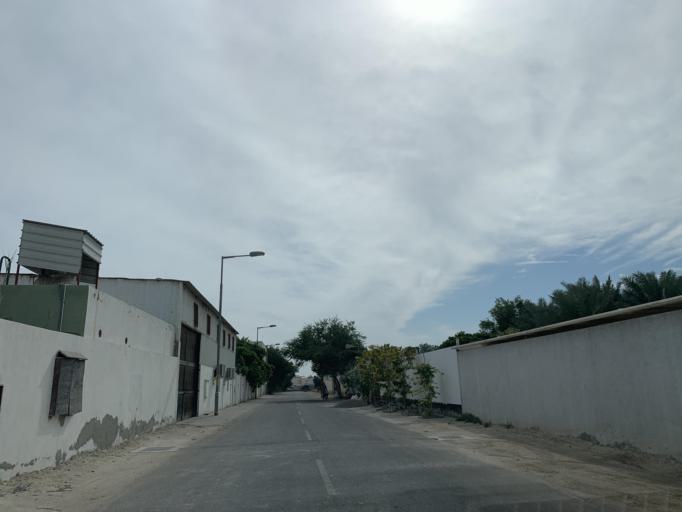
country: BH
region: Central Governorate
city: Madinat Hamad
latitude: 26.1136
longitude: 50.4727
